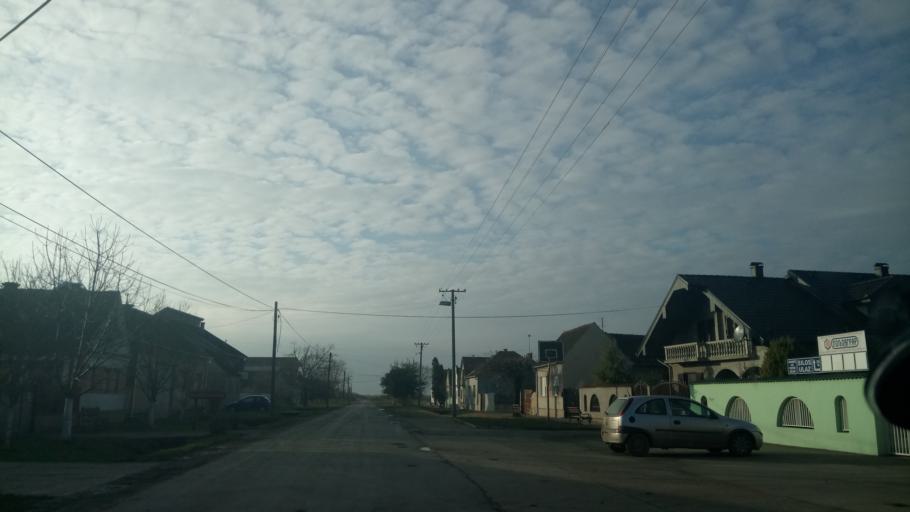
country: RS
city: Vojka
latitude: 44.9369
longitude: 20.1321
